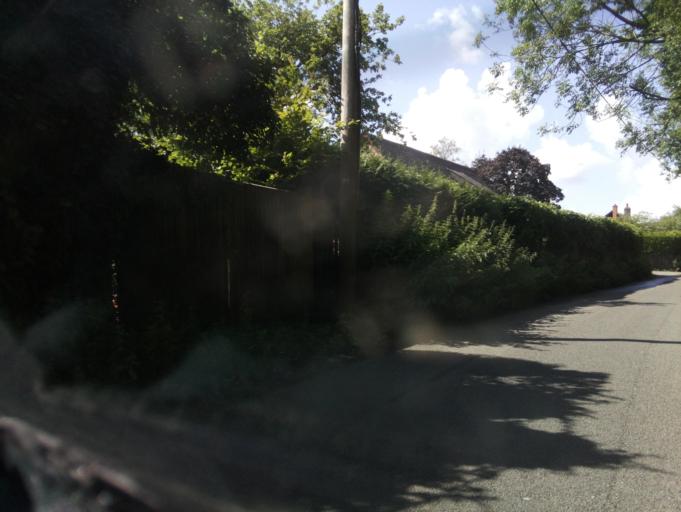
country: GB
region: England
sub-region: Hampshire
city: Kingsclere
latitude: 51.3440
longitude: -1.2807
